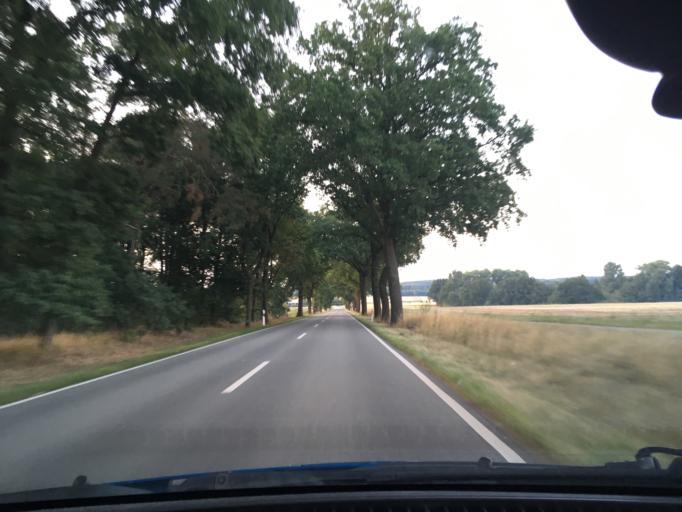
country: DE
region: Lower Saxony
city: Barnstedt
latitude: 53.1279
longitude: 10.4035
